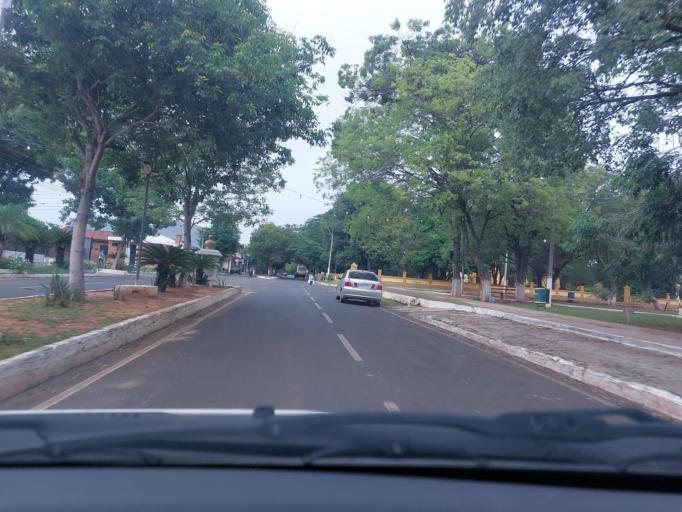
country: PY
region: San Pedro
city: Guayaybi
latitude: -24.6634
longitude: -56.4419
